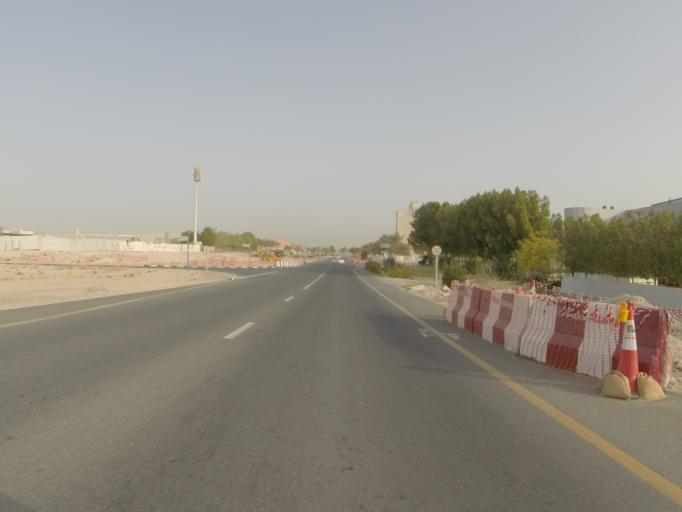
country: AE
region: Dubai
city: Dubai
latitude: 24.9544
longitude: 55.0646
